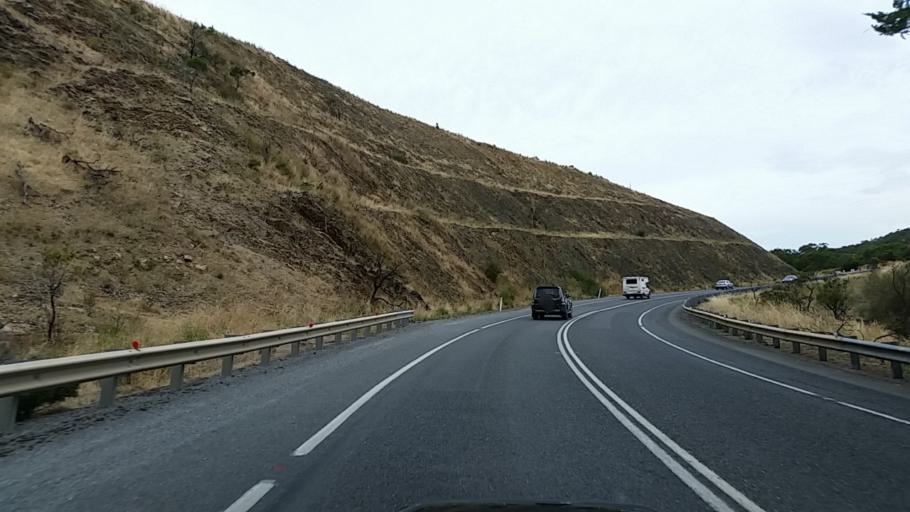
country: AU
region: South Australia
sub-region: Onkaparinga
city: Aldinga
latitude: -35.3636
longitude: 138.4555
